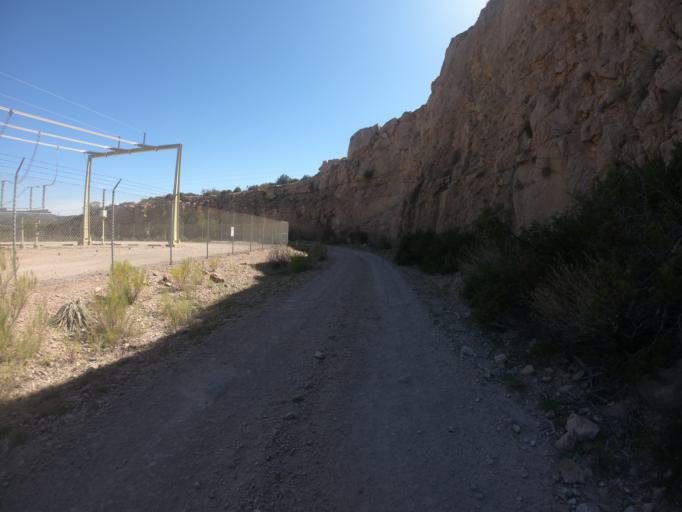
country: US
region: Arizona
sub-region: Pinal County
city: Superior
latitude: 33.3389
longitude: -111.0408
